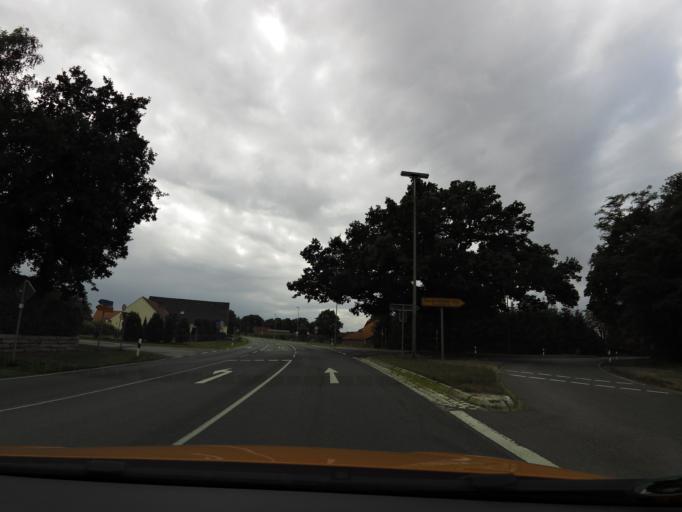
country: DE
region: Lower Saxony
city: Delmenhorst
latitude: 53.0167
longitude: 8.6068
